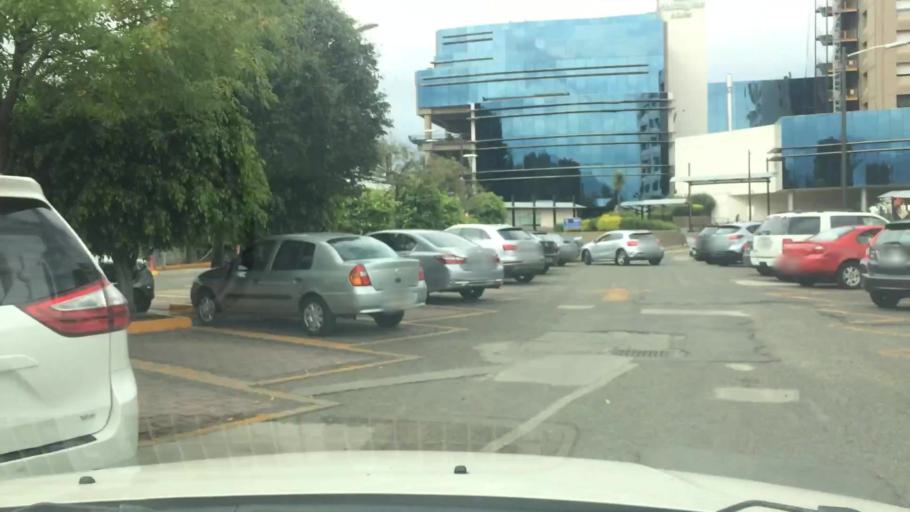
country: MX
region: Mexico City
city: Tlalpan
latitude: 19.2966
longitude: -99.1620
